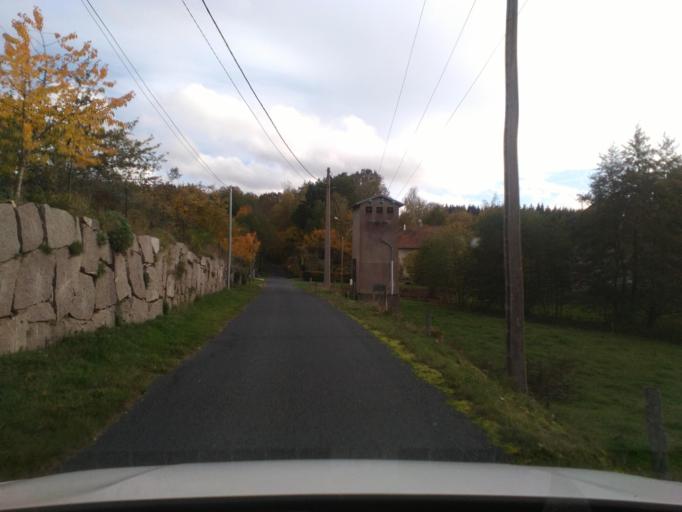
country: FR
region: Lorraine
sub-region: Departement des Vosges
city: Senones
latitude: 48.3535
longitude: 7.0204
